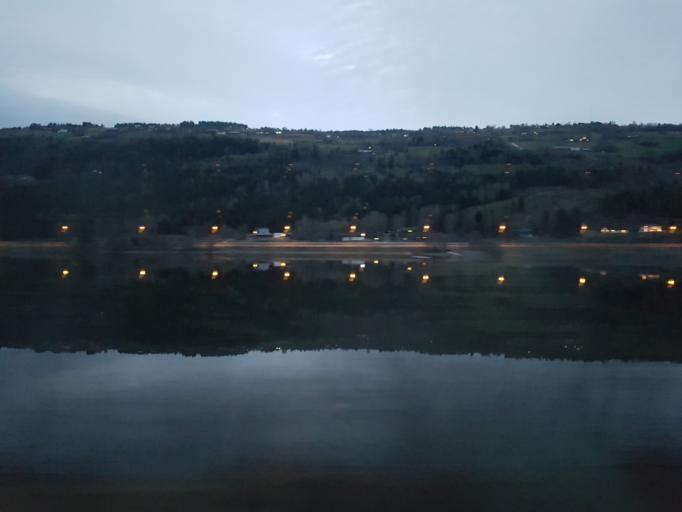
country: NO
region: Oppland
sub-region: Oyer
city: Tretten
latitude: 61.2687
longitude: 10.3969
